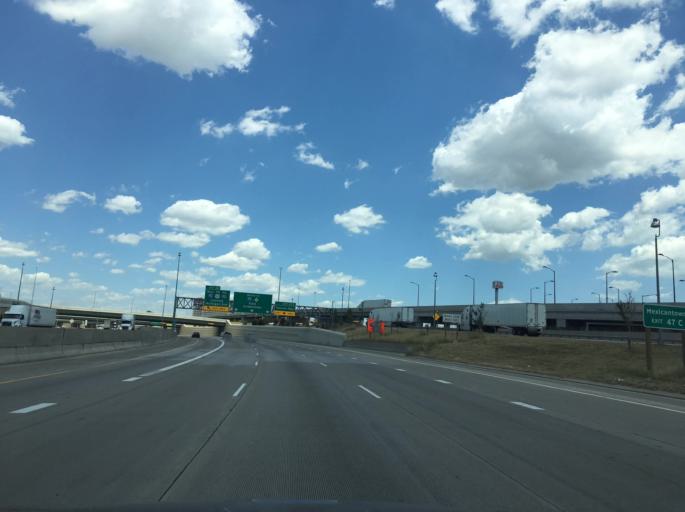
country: US
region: Michigan
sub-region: Wayne County
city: Detroit
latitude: 42.3176
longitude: -83.0830
